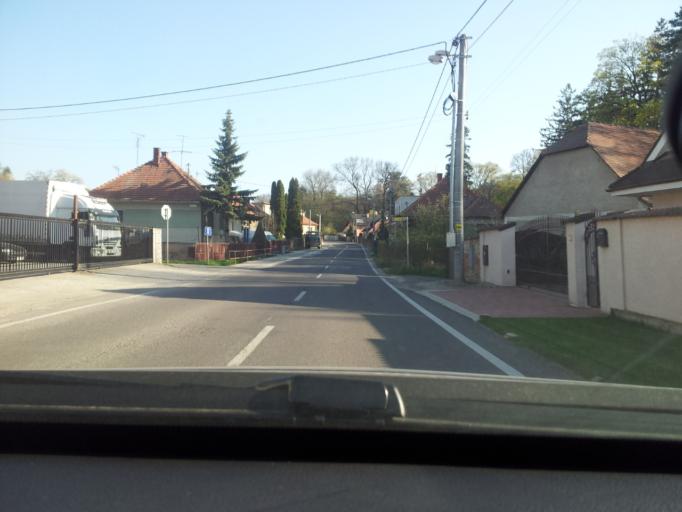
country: SK
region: Nitriansky
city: Zlate Moravce
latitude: 48.4248
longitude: 18.4111
